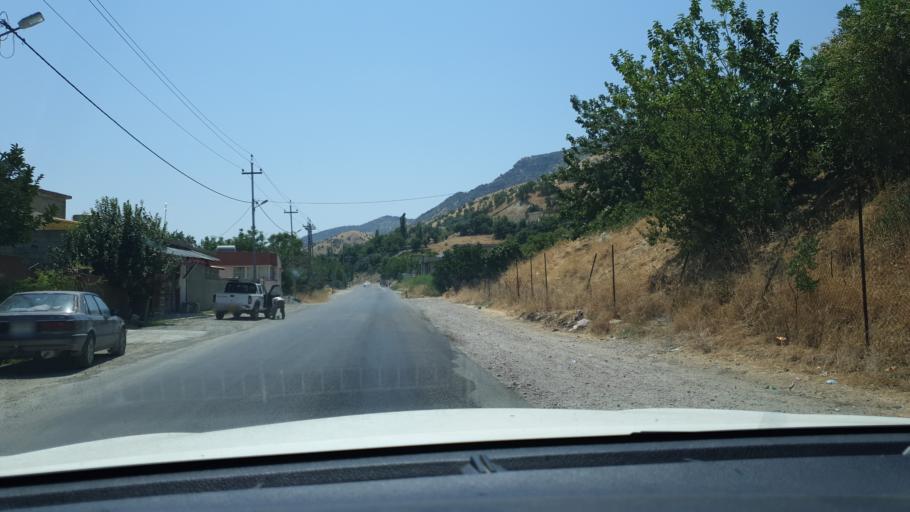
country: IQ
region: Arbil
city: Nahiyat Hiran
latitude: 36.2952
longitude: 44.4747
